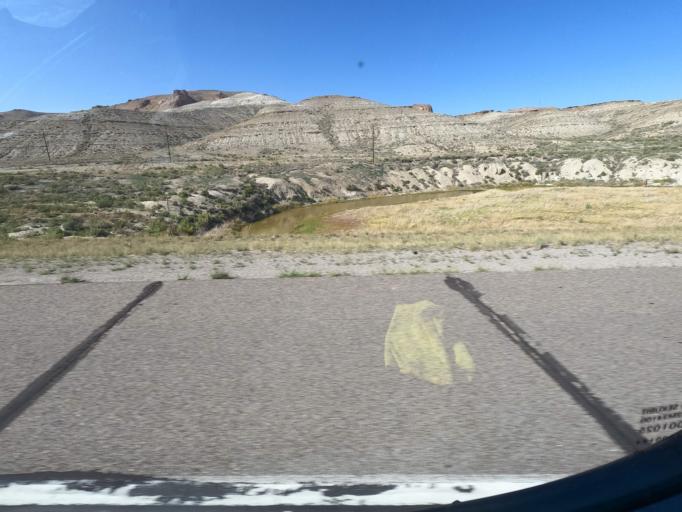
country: US
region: Wyoming
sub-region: Sweetwater County
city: Green River
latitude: 41.5332
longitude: -109.3858
